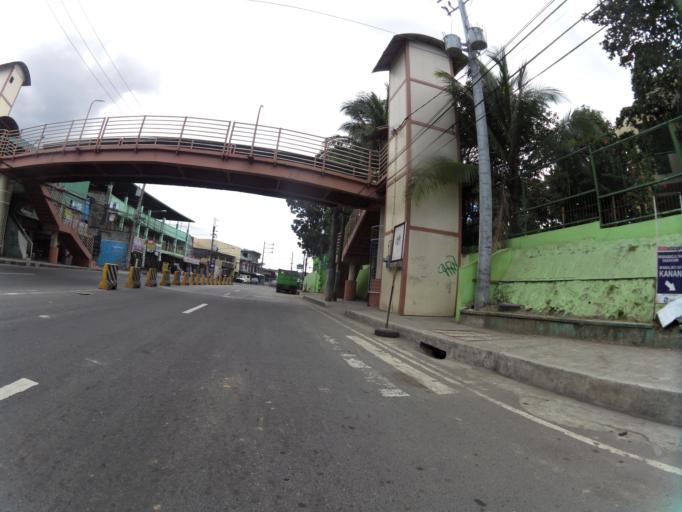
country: PH
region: Calabarzon
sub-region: Province of Rizal
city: Antipolo
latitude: 14.6295
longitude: 121.1209
